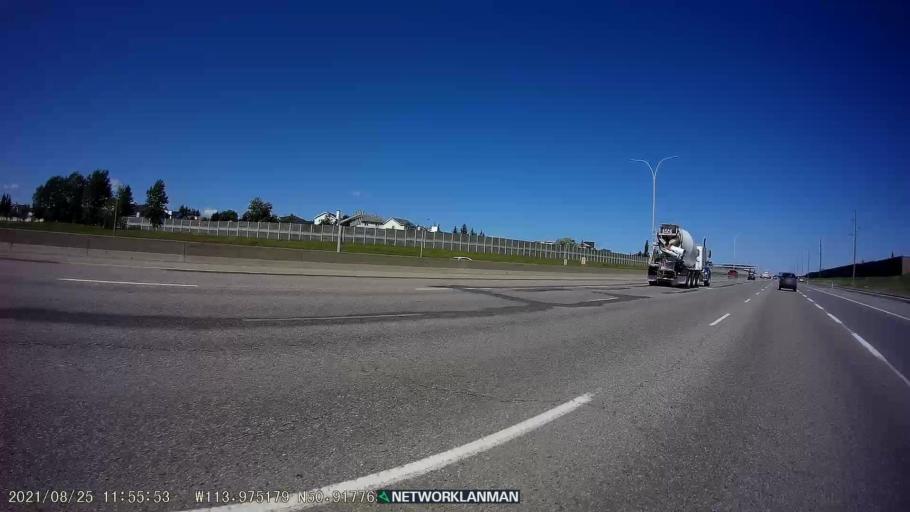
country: CA
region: Alberta
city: Calgary
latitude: 50.9176
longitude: -113.9743
